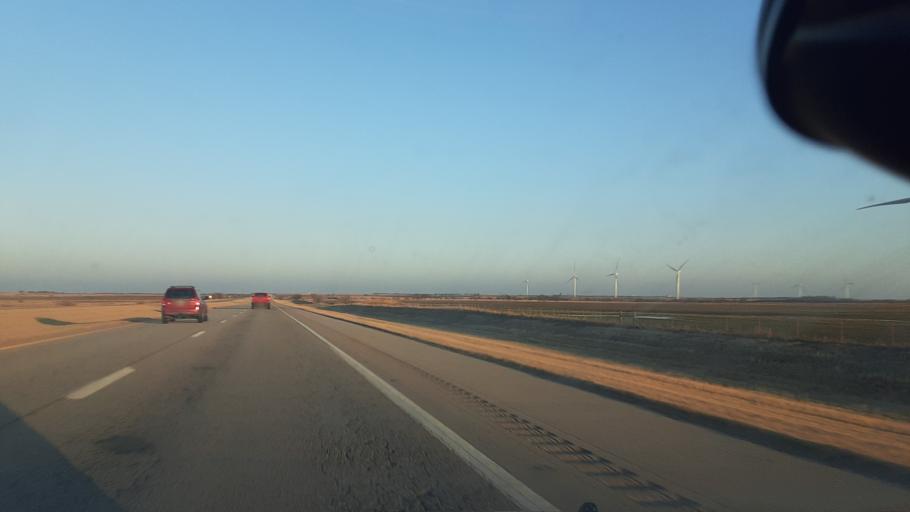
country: US
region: Oklahoma
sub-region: Noble County
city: Perry
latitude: 36.3978
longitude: -97.4076
